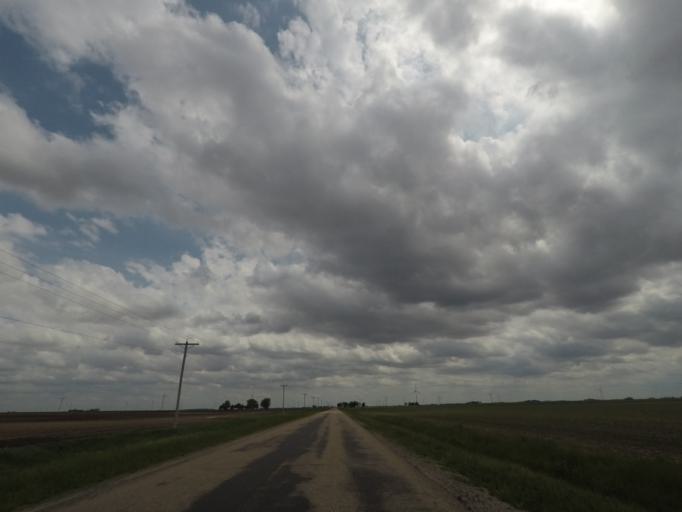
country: US
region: Illinois
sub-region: Macon County
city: Maroa
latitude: 40.0683
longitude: -89.0860
